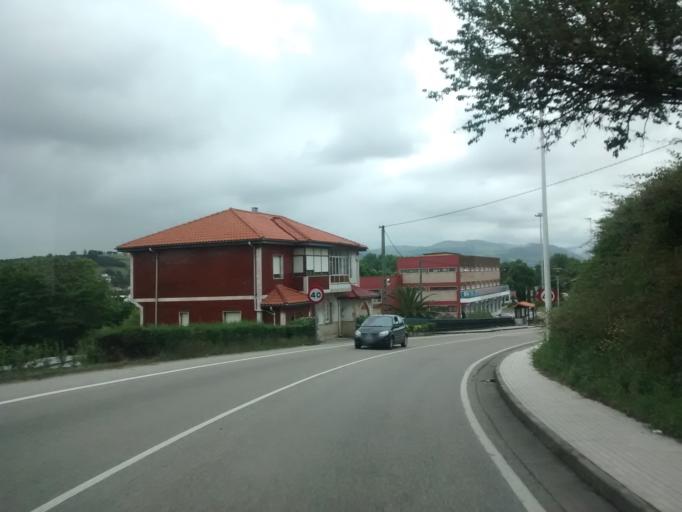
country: ES
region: Cantabria
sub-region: Provincia de Cantabria
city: Torrelavega
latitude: 43.3796
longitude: -4.0481
